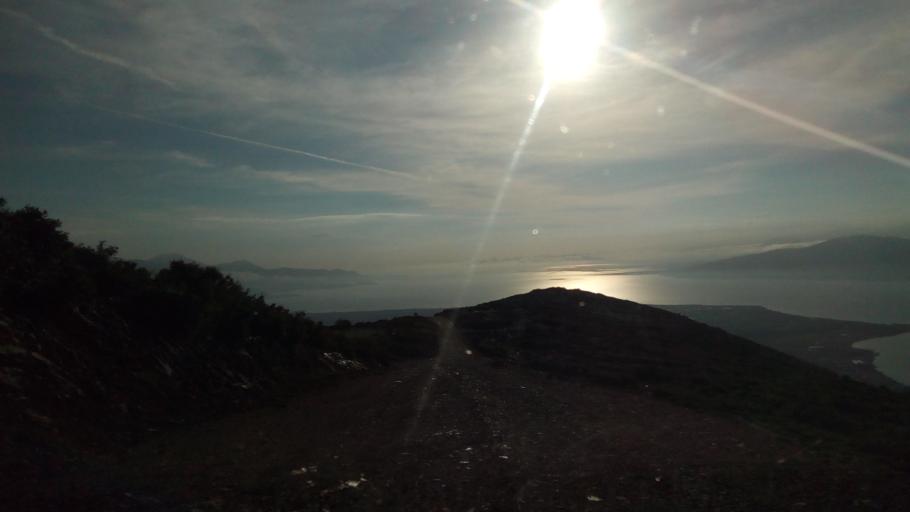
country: GR
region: West Greece
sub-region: Nomos Aitolias kai Akarnanias
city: Nafpaktos
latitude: 38.4157
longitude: 21.8132
